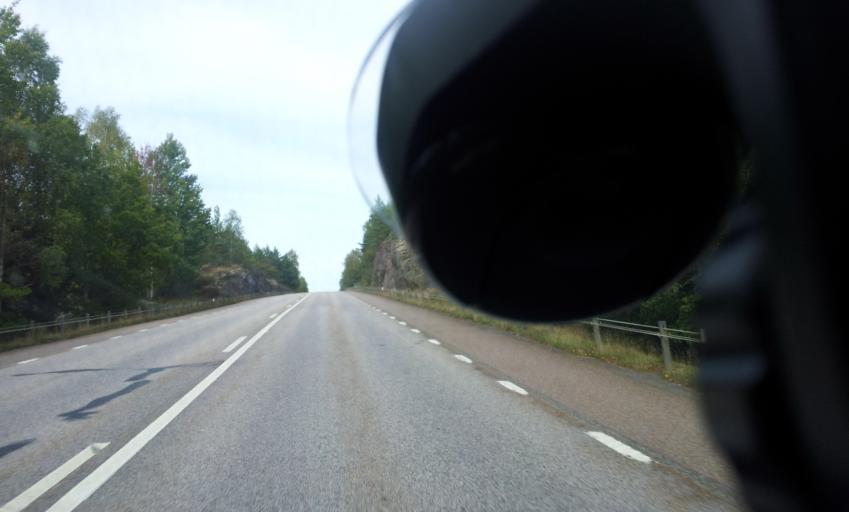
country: SE
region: Kalmar
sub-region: Oskarshamns Kommun
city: Oskarshamn
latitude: 57.5041
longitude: 16.5030
